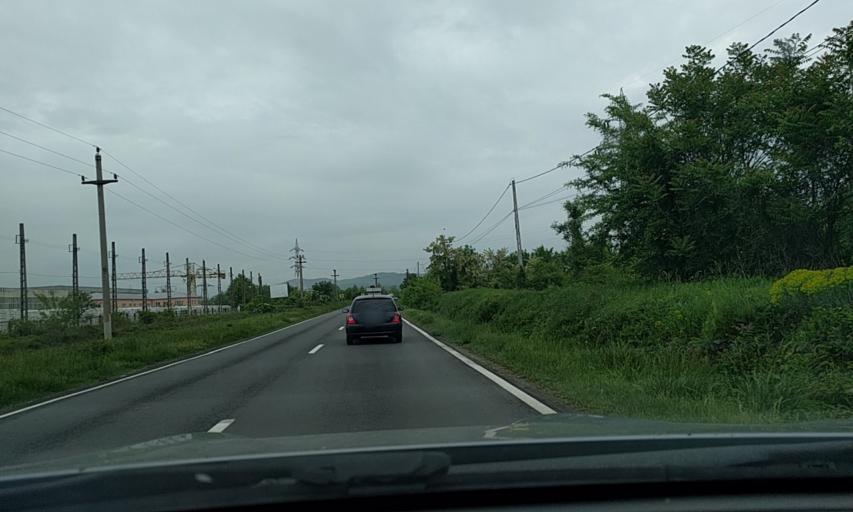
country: RO
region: Dambovita
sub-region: Comuna Vulcana-Pandele
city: Vulcana-Pandele
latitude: 45.0063
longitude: 25.4014
